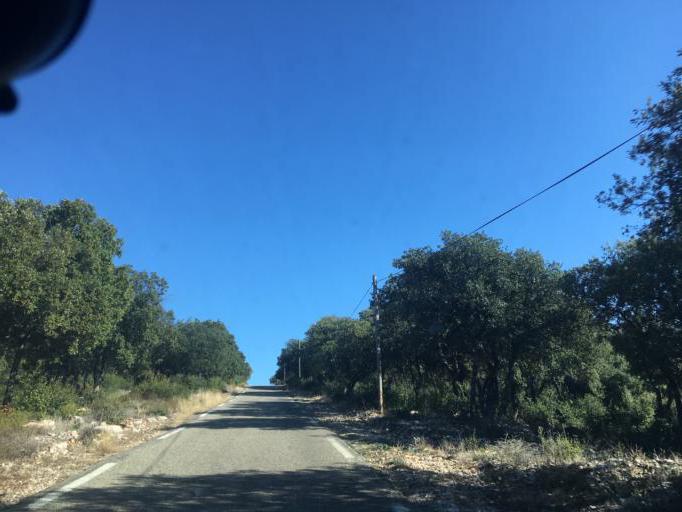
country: FR
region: Provence-Alpes-Cote d'Azur
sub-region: Departement du Var
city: Regusse
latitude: 43.7278
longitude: 6.1195
